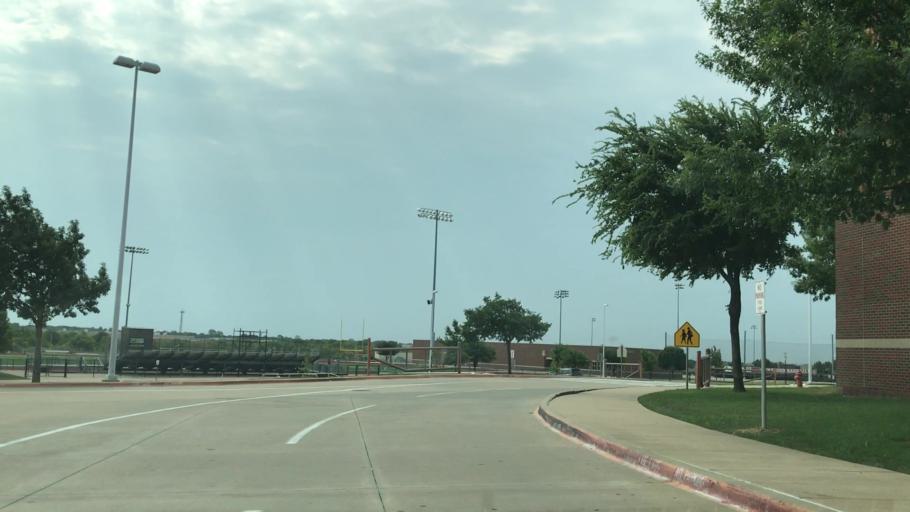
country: US
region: Texas
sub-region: Tarrant County
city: Keller
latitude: 32.9106
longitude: -97.2692
